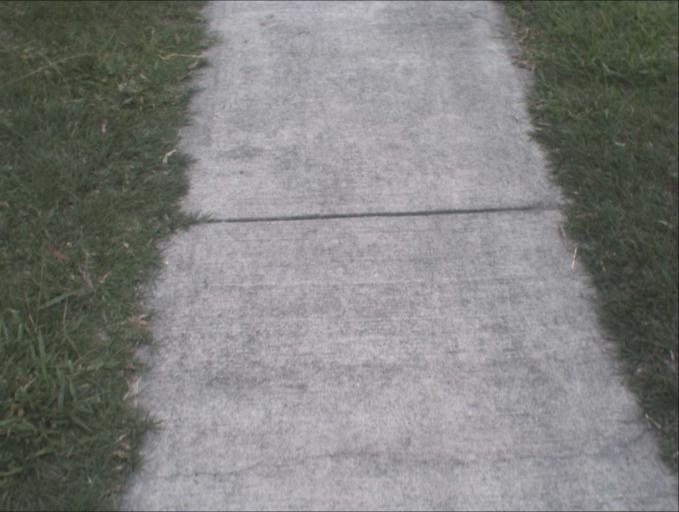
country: AU
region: Queensland
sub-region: Logan
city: Park Ridge South
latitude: -27.6966
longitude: 153.0366
